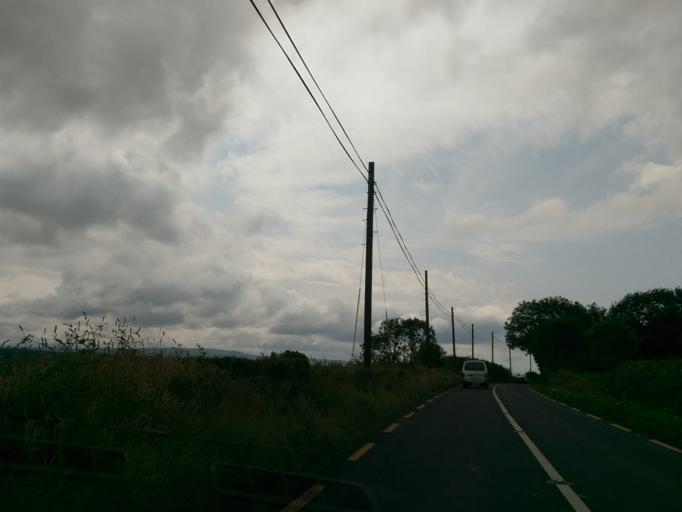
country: IE
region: Munster
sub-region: An Clar
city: Kilrush
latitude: 52.6539
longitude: -9.4455
